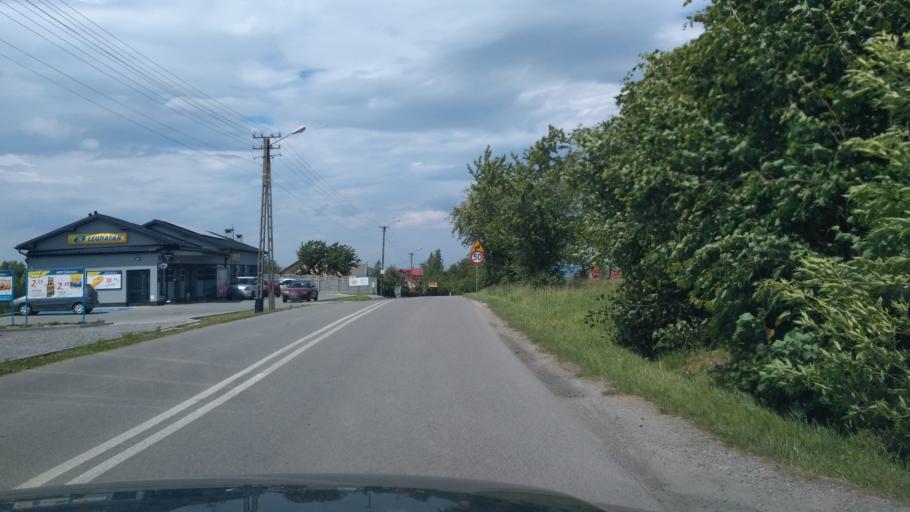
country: PL
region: Subcarpathian Voivodeship
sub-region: Powiat ropczycko-sedziszowski
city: Ropczyce
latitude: 50.0346
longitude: 21.6199
